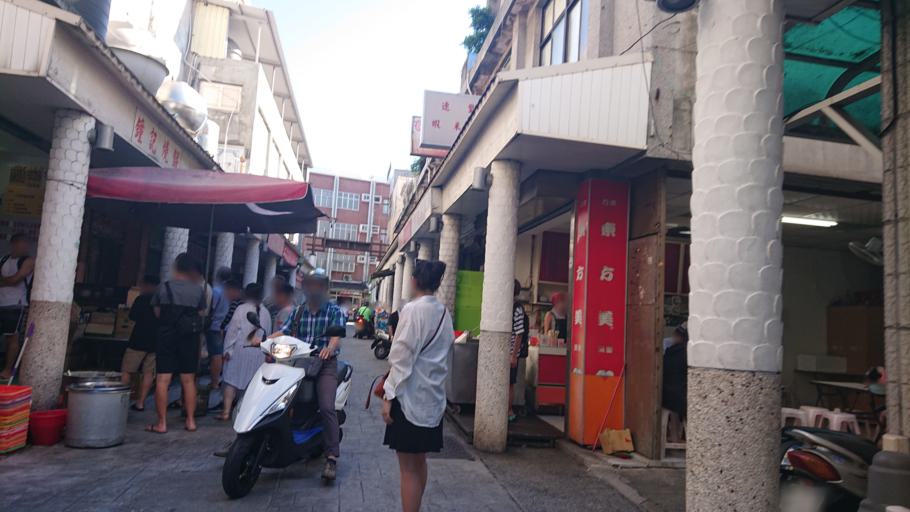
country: TW
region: Taiwan
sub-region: Penghu
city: Ma-kung
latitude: 23.5684
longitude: 119.5672
